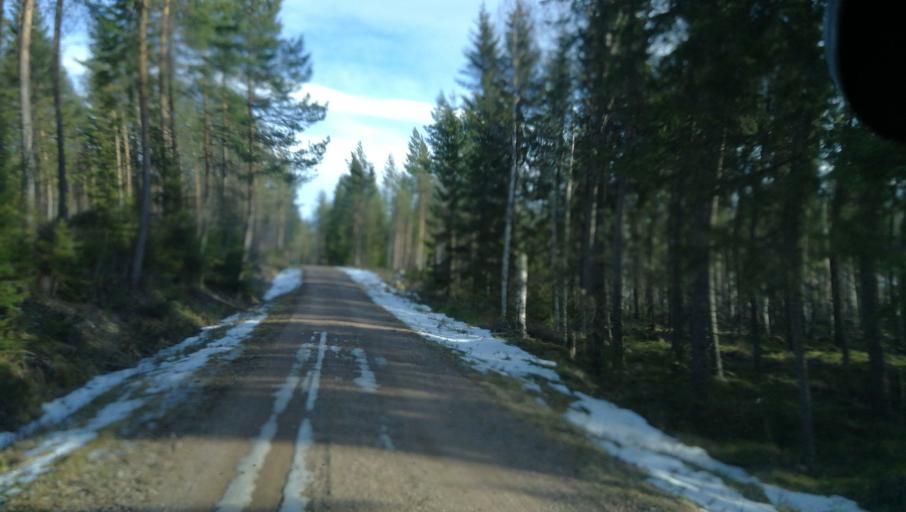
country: SE
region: Dalarna
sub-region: Vansbro Kommun
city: Vansbro
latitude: 60.7983
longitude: 14.2222
